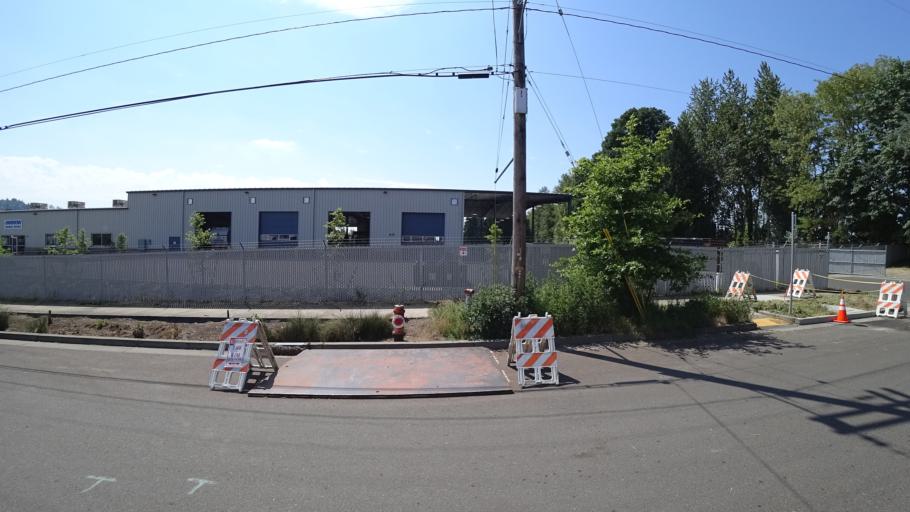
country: US
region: Oregon
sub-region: Multnomah County
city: Lents
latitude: 45.5635
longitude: -122.5507
